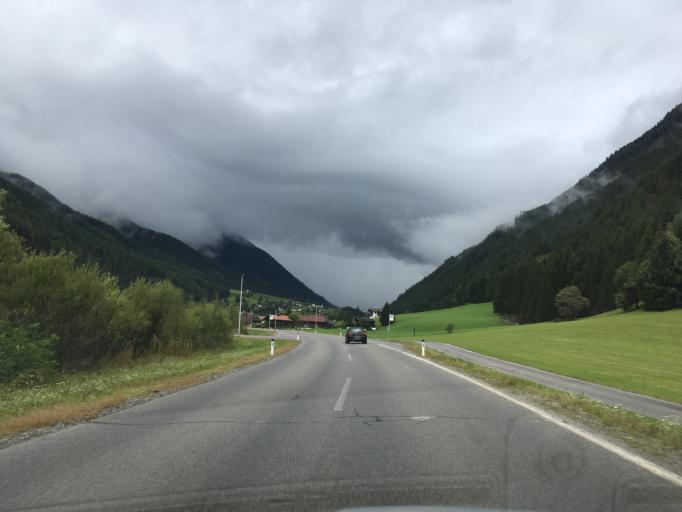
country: AT
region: Tyrol
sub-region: Politischer Bezirk Lienz
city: Virgen
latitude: 46.9171
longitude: 12.3936
